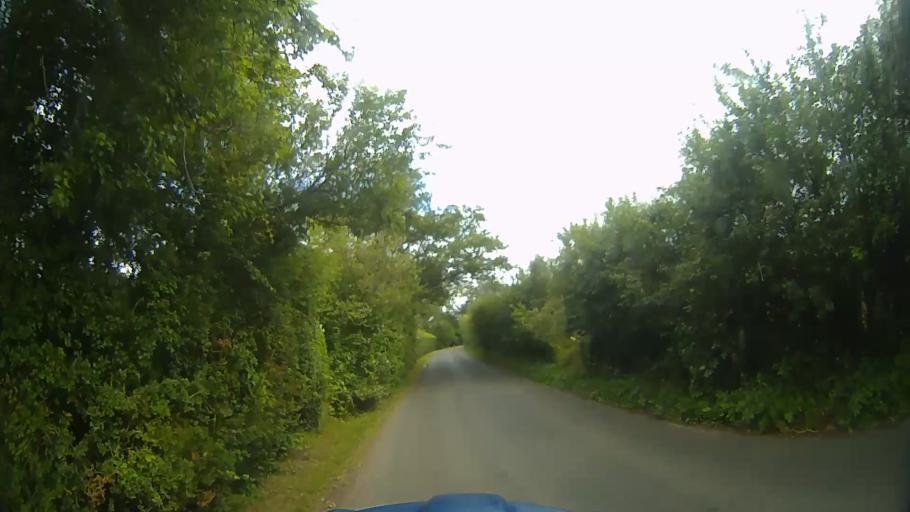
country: GB
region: England
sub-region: Hampshire
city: Basingstoke
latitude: 51.3105
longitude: -1.0672
